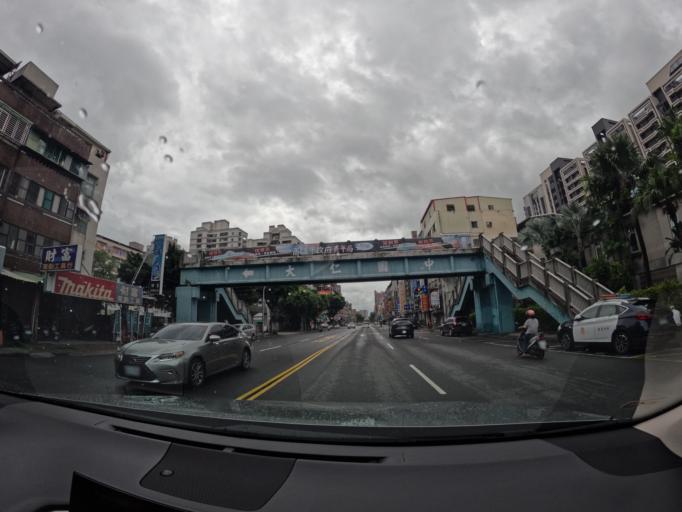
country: TW
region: Kaohsiung
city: Kaohsiung
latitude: 22.6329
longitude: 120.3288
